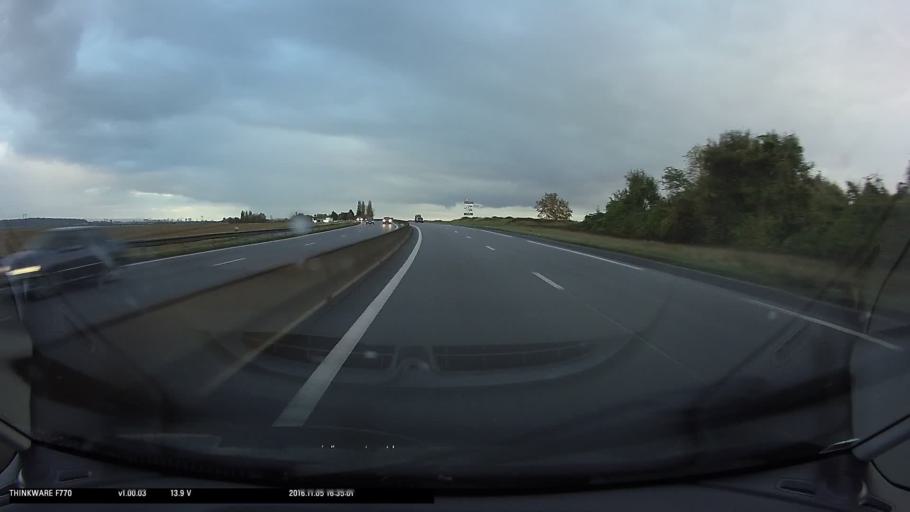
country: FR
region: Ile-de-France
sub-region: Departement du Val-d'Oise
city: Ableiges
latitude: 49.0673
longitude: 1.9723
